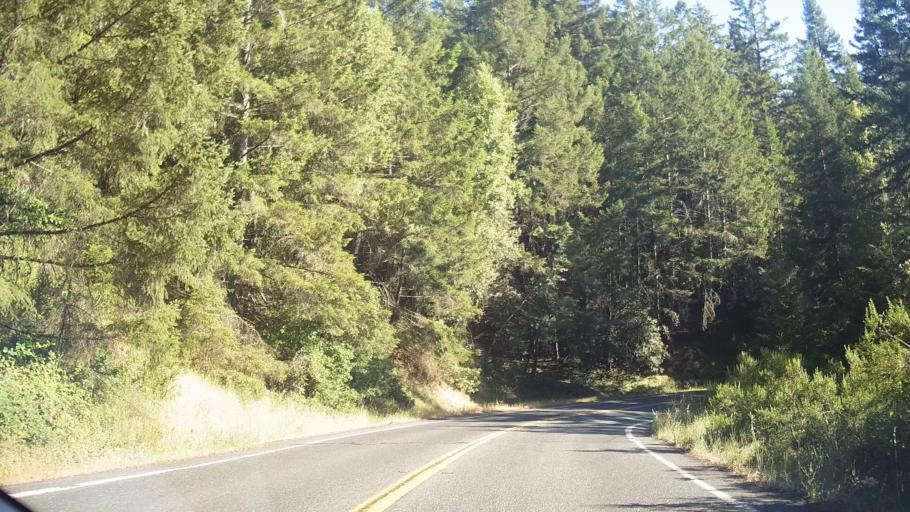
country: US
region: California
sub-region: Mendocino County
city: Brooktrails
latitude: 39.3963
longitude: -123.4536
